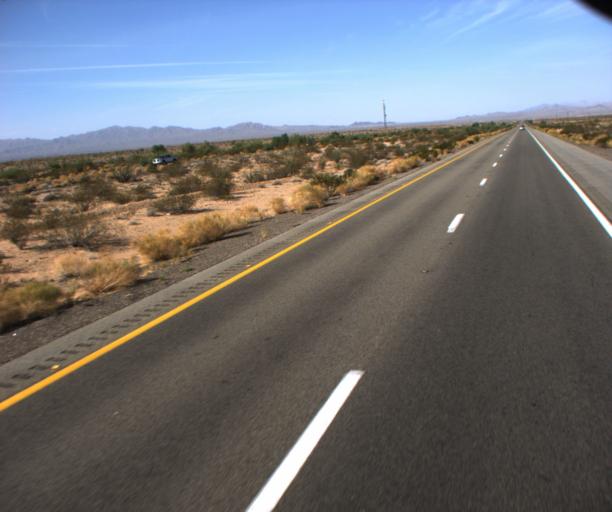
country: US
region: Arizona
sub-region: Mohave County
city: Desert Hills
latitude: 34.7819
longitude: -114.1792
